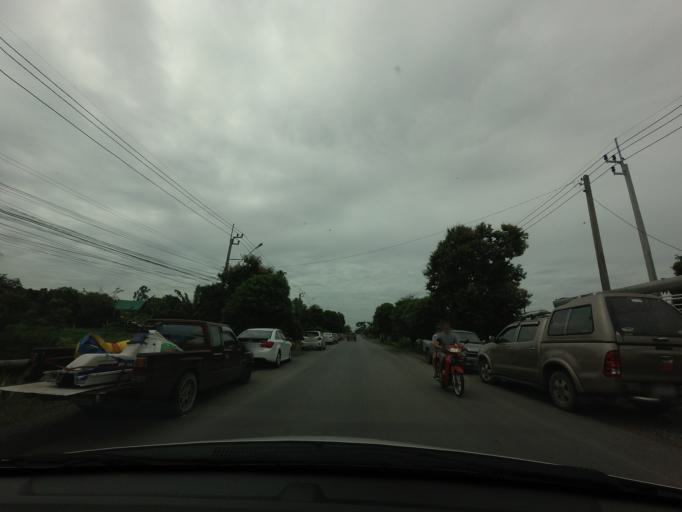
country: TH
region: Bangkok
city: Nong Chok
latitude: 13.8725
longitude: 100.8086
